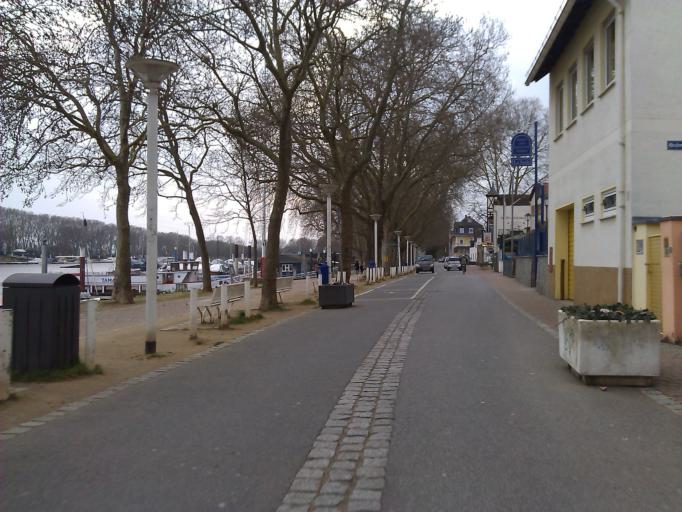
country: DE
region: Rheinland-Pfalz
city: Budenheim
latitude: 50.0423
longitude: 8.1988
